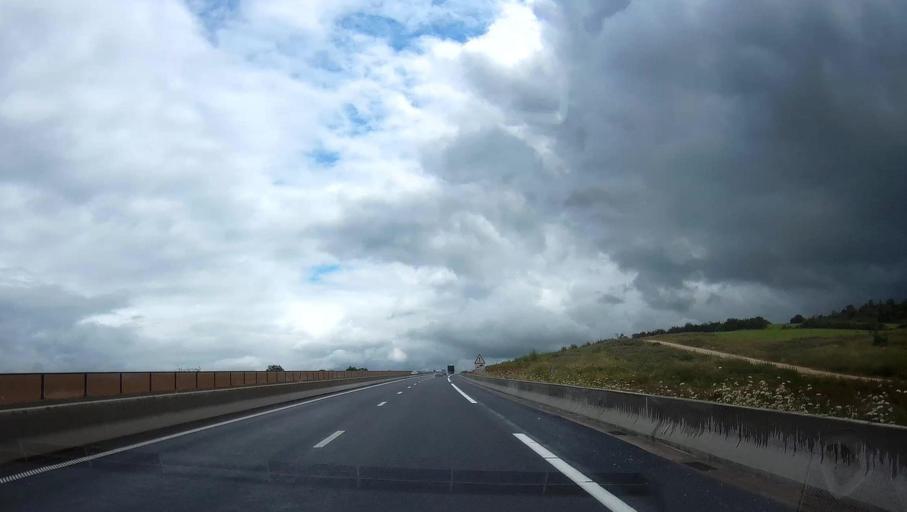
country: FR
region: Champagne-Ardenne
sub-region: Departement des Ardennes
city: Tournes
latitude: 49.7840
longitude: 4.6001
